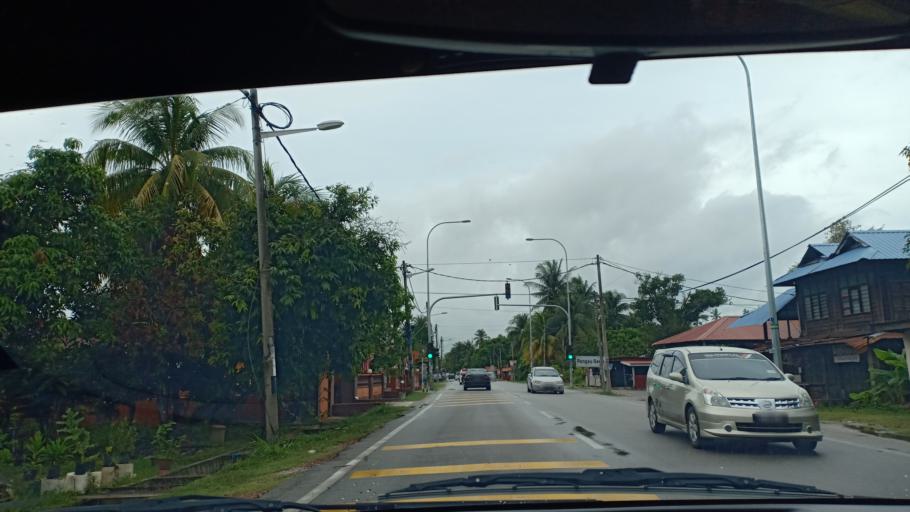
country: MY
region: Penang
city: Kepala Batas
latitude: 5.4970
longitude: 100.4435
